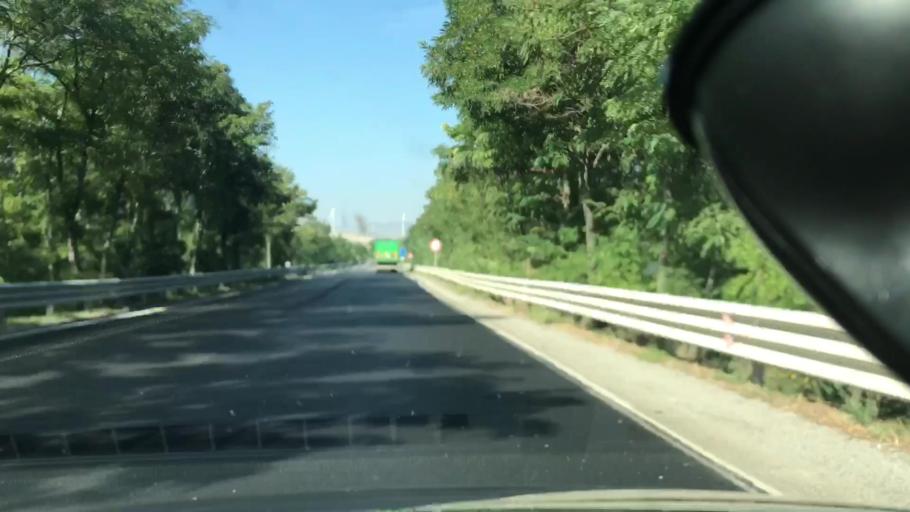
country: IT
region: Basilicate
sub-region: Provincia di Potenza
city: Zona 179
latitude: 41.0824
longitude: 15.6170
